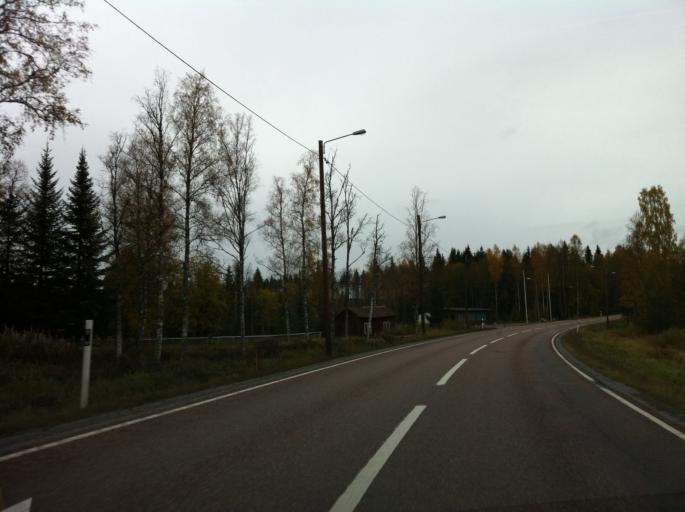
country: SE
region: Dalarna
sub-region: Ludvika Kommun
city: Grangesberg
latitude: 60.0333
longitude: 14.9716
